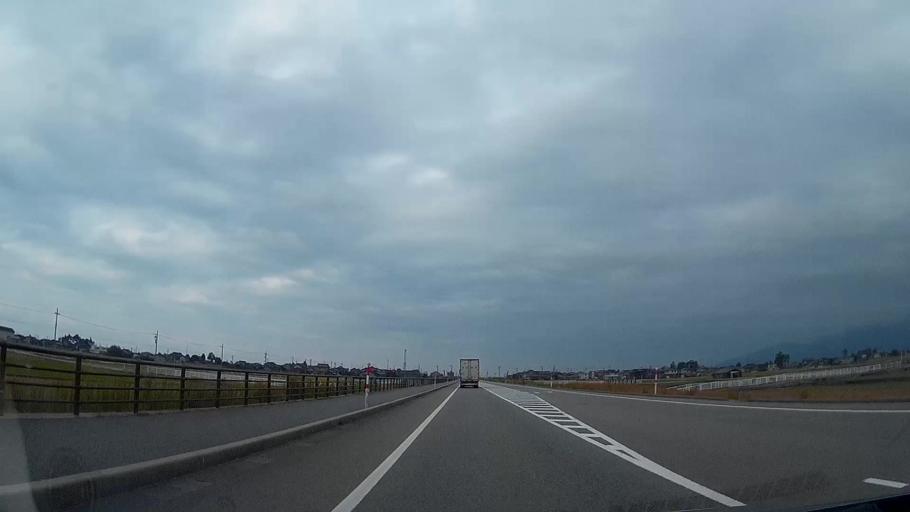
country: JP
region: Toyama
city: Nyuzen
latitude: 36.9175
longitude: 137.4632
